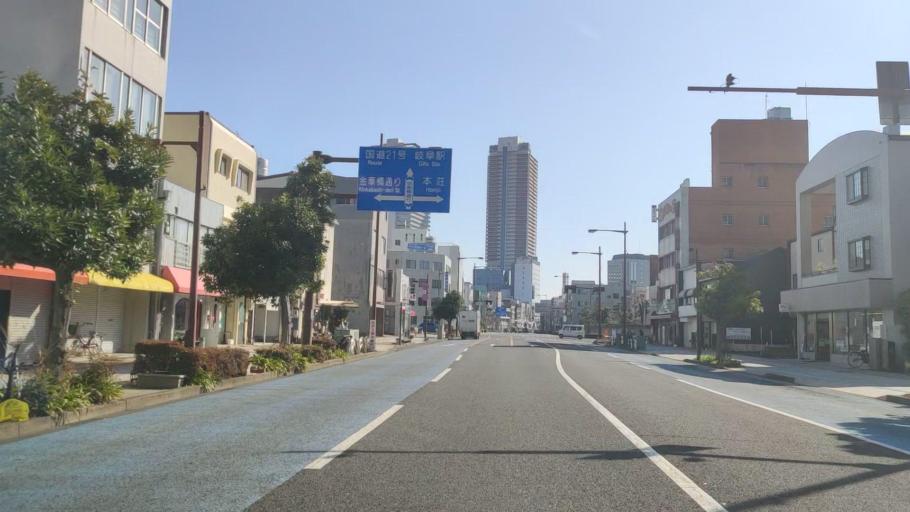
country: JP
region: Gifu
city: Gifu-shi
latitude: 35.4159
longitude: 136.7532
